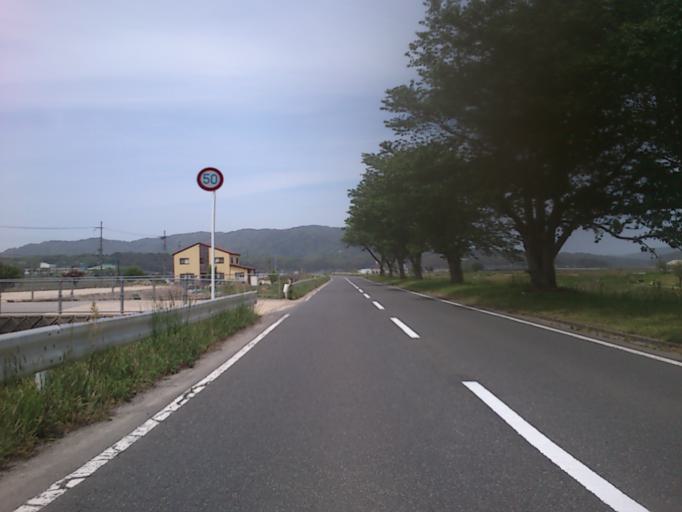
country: JP
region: Kyoto
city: Miyazu
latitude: 35.6617
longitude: 135.0866
